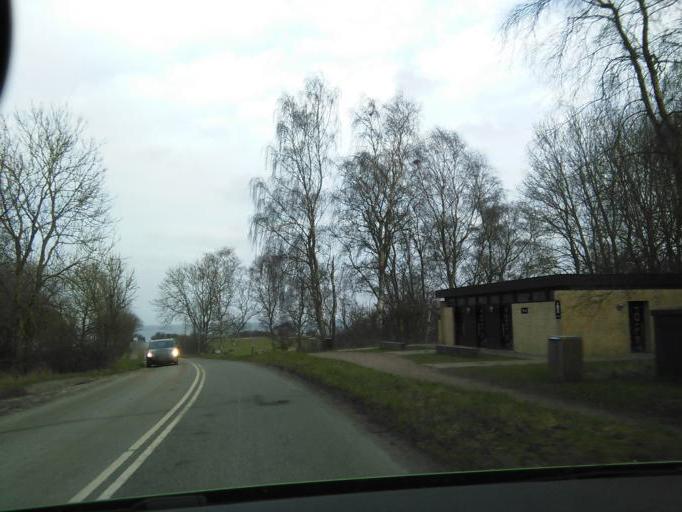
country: DK
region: Central Jutland
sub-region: Arhus Kommune
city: Beder
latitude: 56.0888
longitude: 10.2445
